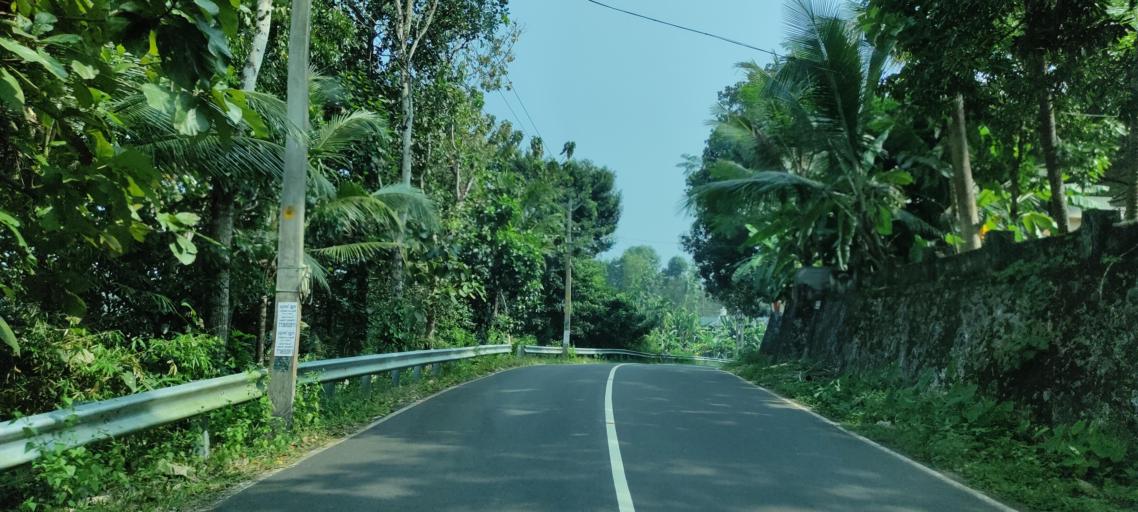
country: IN
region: Kerala
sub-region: Pattanamtitta
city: Adur
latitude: 9.2322
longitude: 76.6967
